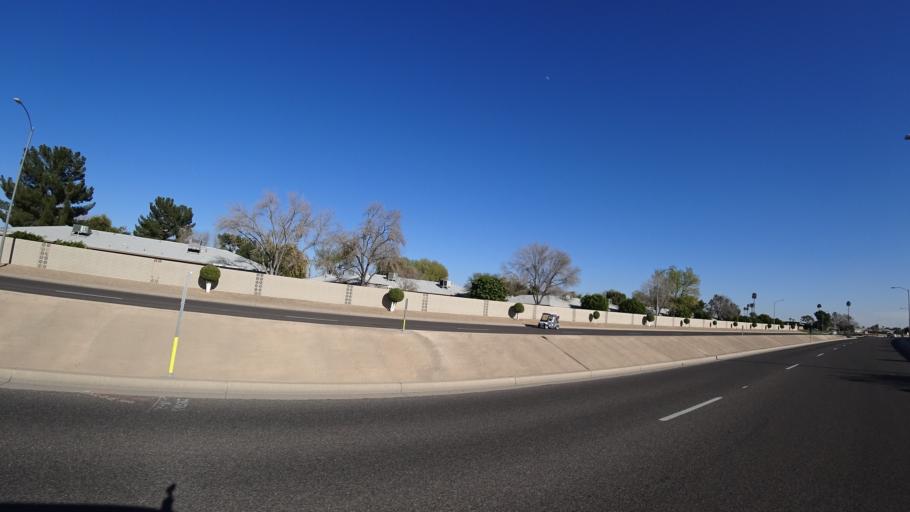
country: US
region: Arizona
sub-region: Maricopa County
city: Sun City West
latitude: 33.6733
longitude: -112.3358
